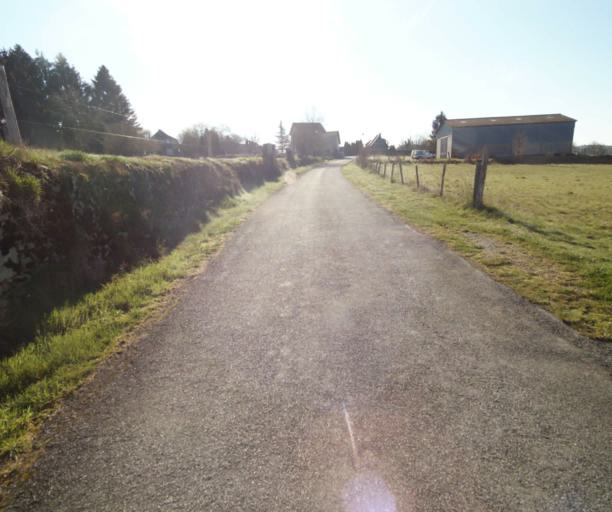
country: FR
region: Limousin
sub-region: Departement de la Correze
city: Correze
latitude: 45.3160
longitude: 1.8867
